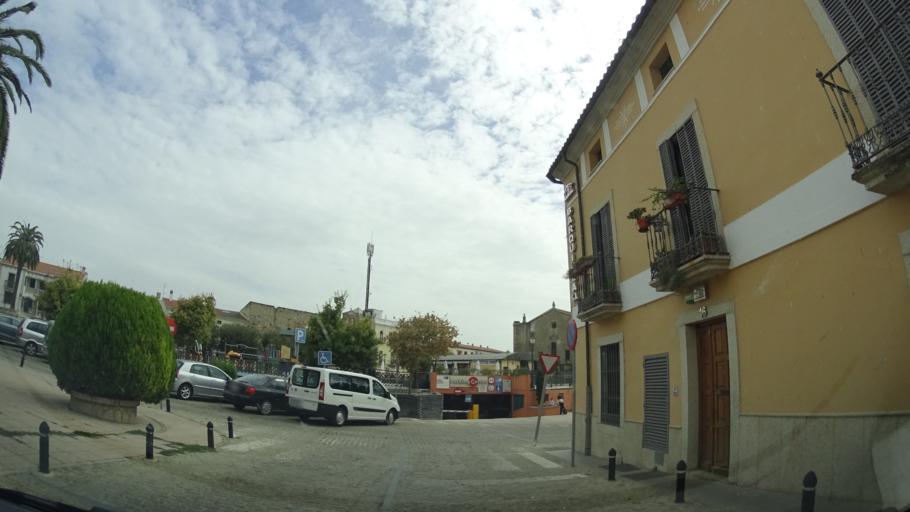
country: ES
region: Extremadura
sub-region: Provincia de Caceres
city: Trujillo
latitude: 39.4575
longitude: -5.8827
